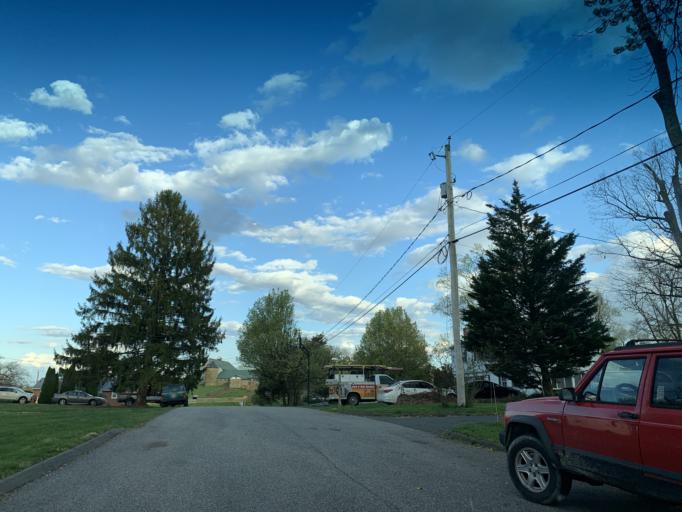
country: US
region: Maryland
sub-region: Harford County
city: South Bel Air
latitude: 39.5994
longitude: -76.3219
